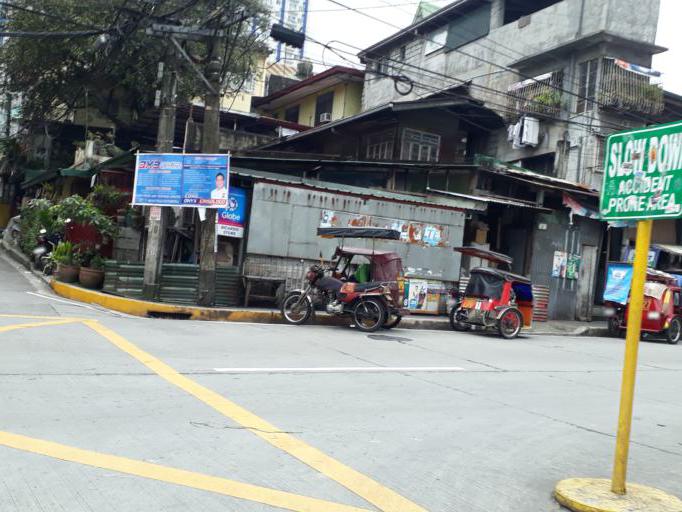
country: PH
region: Calabarzon
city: Bagong Pagasa
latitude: 14.6620
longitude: 121.0283
